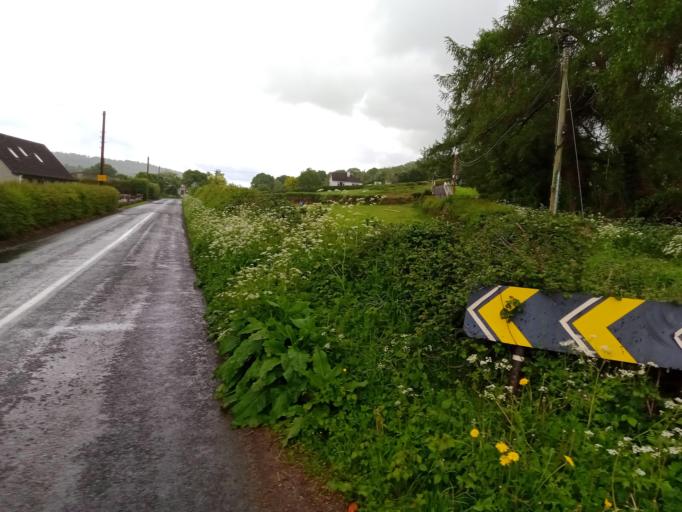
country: IE
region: Leinster
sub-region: Kilkenny
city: Thomastown
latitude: 52.5187
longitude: -7.1349
